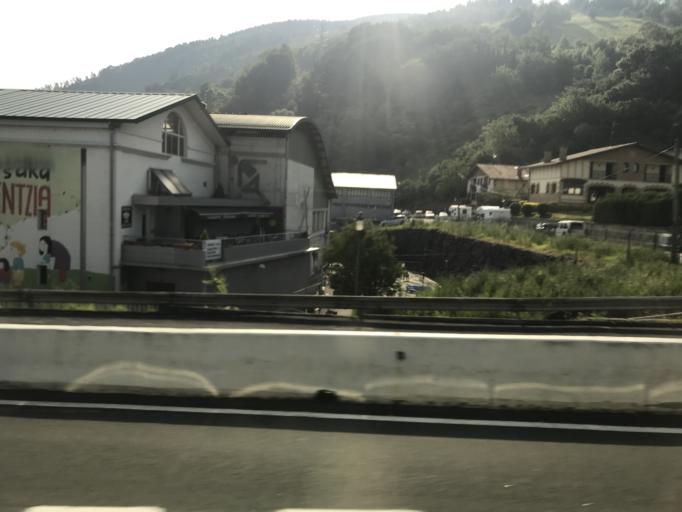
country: ES
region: Basque Country
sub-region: Provincia de Guipuzcoa
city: Irura
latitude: 43.1672
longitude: -2.0662
